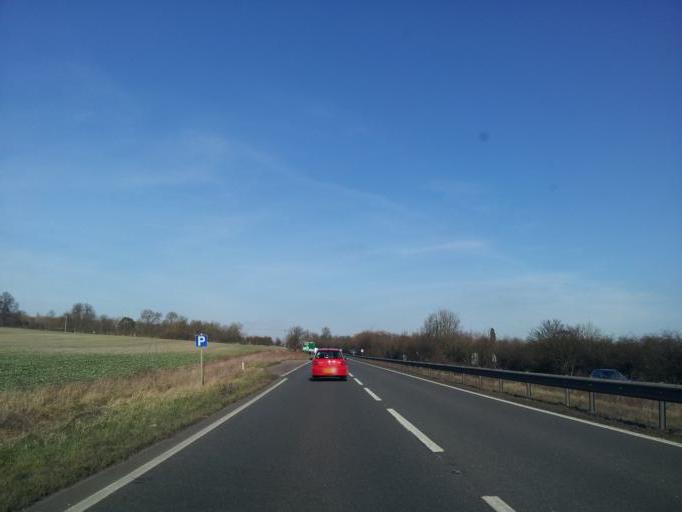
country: GB
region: England
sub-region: Cambridgeshire
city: Little Paxton
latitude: 52.2723
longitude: -0.2604
